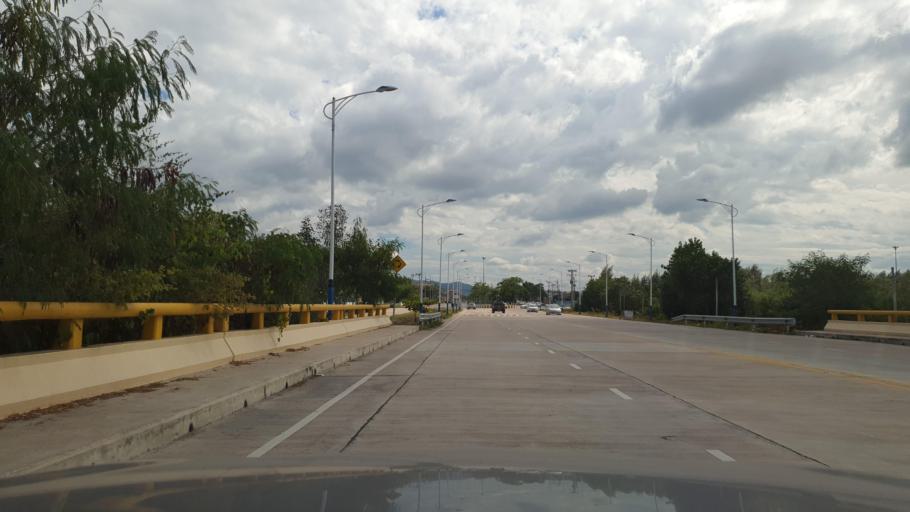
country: TH
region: Chon Buri
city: Chon Buri
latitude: 13.3462
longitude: 100.9494
